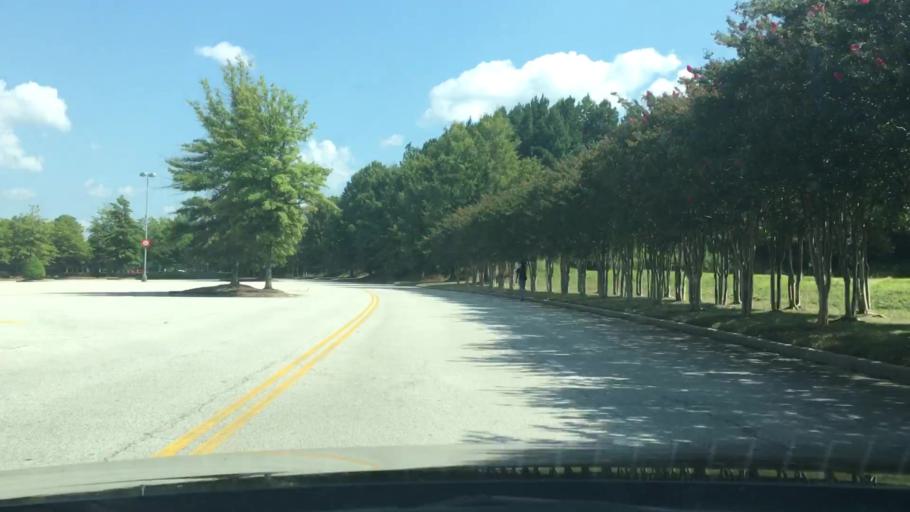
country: US
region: Georgia
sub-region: DeKalb County
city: Lithonia
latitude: 33.6967
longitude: -84.0977
